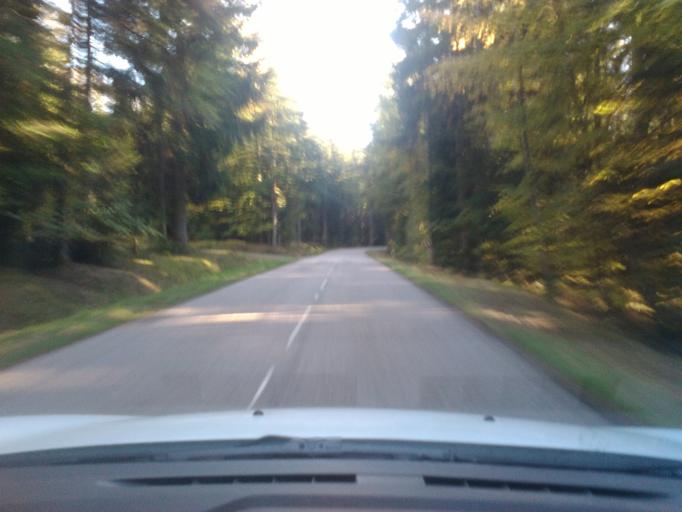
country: FR
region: Lorraine
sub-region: Departement des Vosges
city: Etival-Clairefontaine
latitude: 48.2911
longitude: 6.7851
